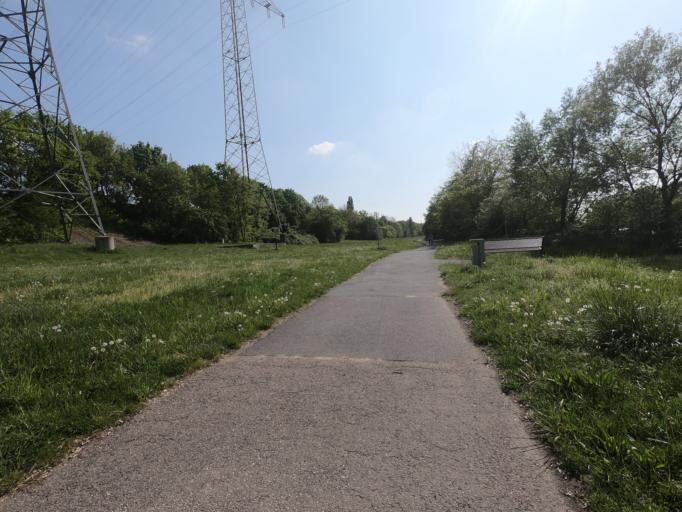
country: DE
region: Hesse
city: Kelsterbach
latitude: 50.0544
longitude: 8.5107
